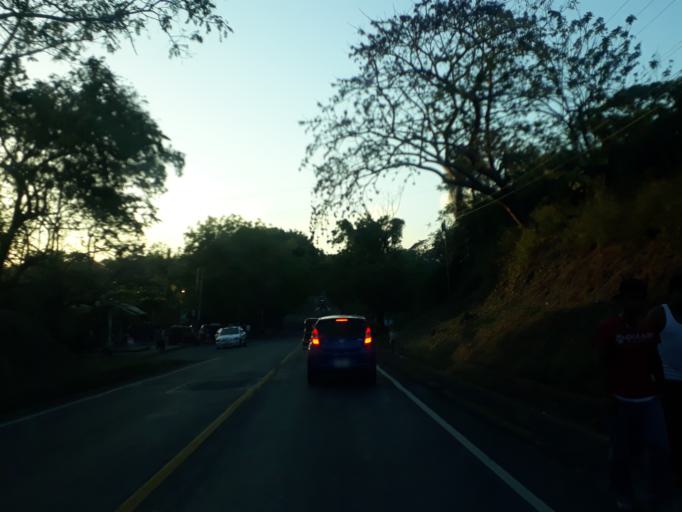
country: NI
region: Masaya
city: Nandasmo
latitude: 11.9012
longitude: -86.1182
